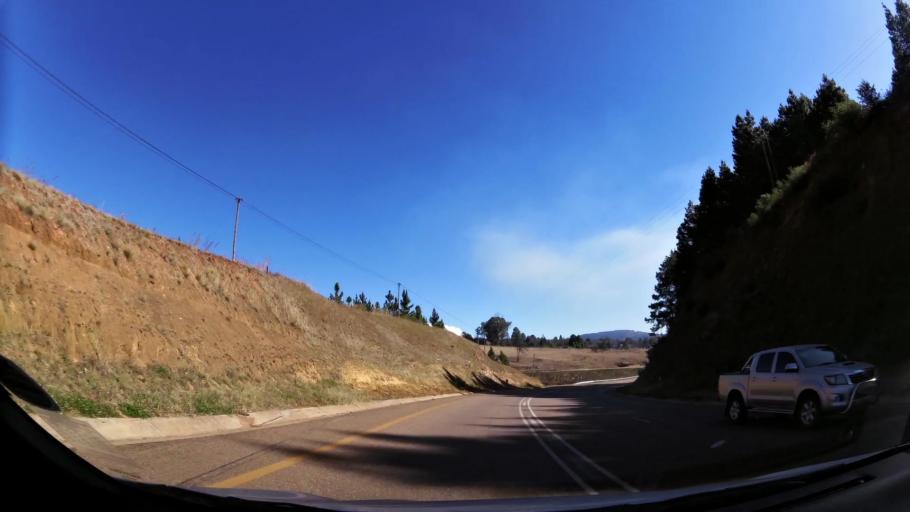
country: ZA
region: Limpopo
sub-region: Capricorn District Municipality
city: Mankoeng
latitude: -23.9394
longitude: 29.9499
